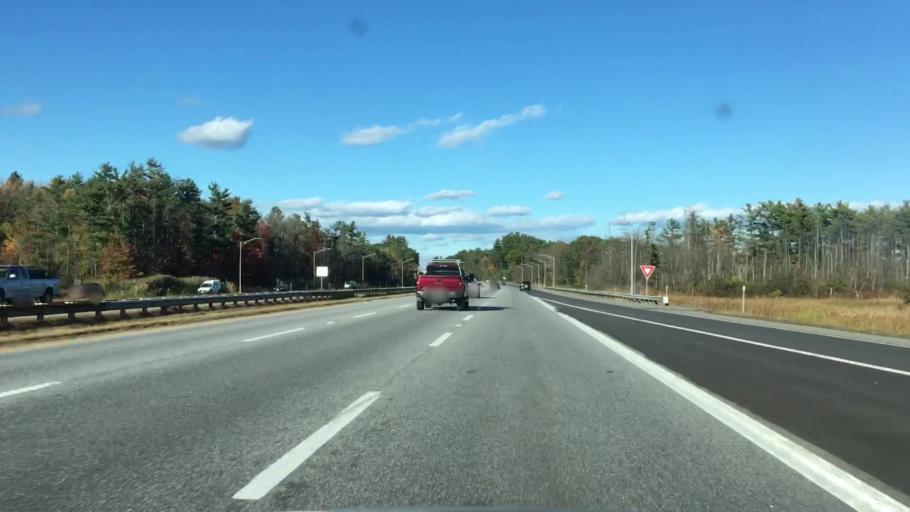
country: US
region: Maine
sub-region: York County
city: Biddeford
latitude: 43.4821
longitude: -70.4979
